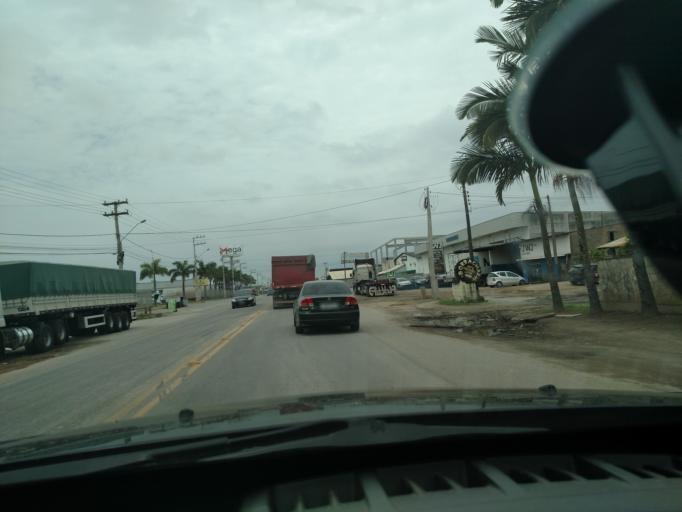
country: BR
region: Santa Catarina
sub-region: Itajai
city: Itajai
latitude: -26.8878
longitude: -48.7326
